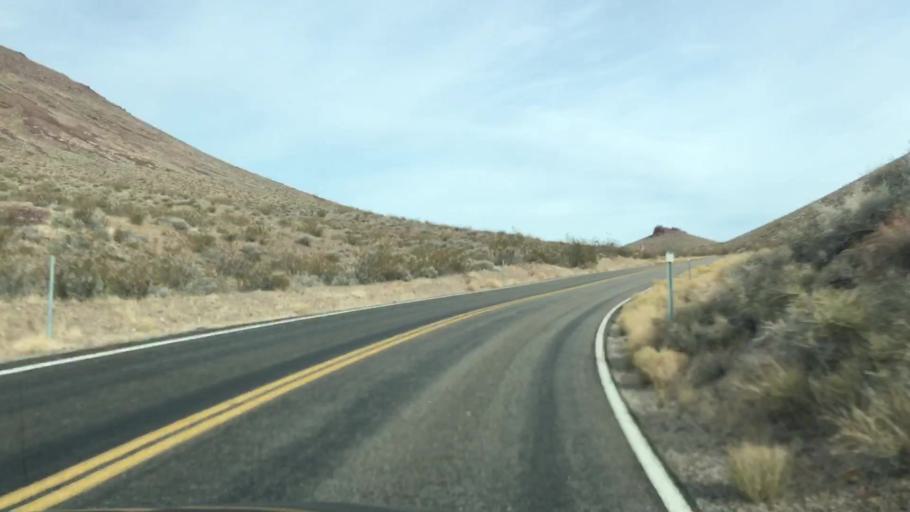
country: US
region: Nevada
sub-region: Nye County
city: Beatty
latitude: 36.7777
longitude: -116.9331
